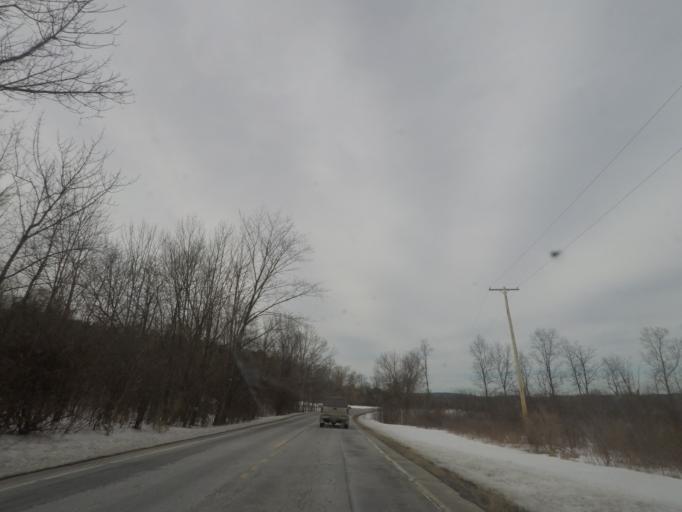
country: US
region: New York
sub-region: Albany County
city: Altamont
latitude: 42.6792
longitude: -74.0182
